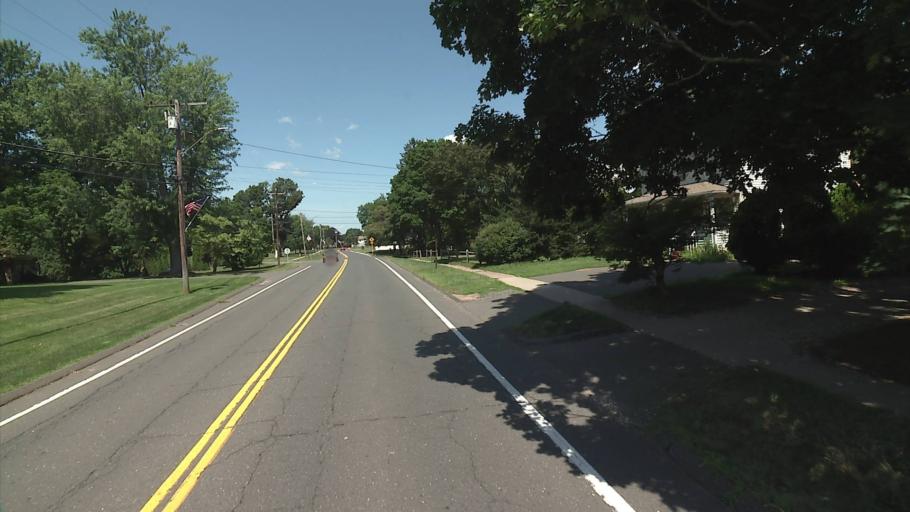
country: US
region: Connecticut
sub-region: Middlesex County
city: Cromwell
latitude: 41.5989
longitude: -72.6522
